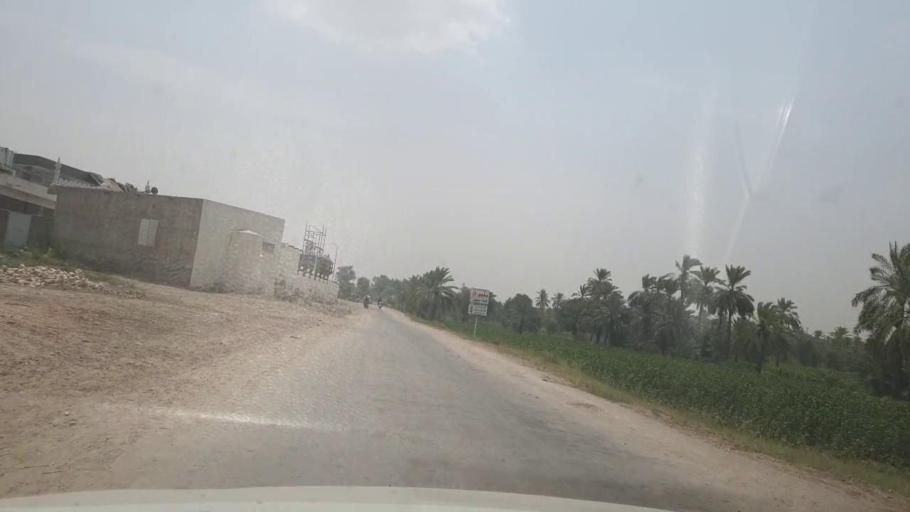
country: PK
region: Sindh
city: Kot Diji
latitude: 27.3691
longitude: 68.7229
